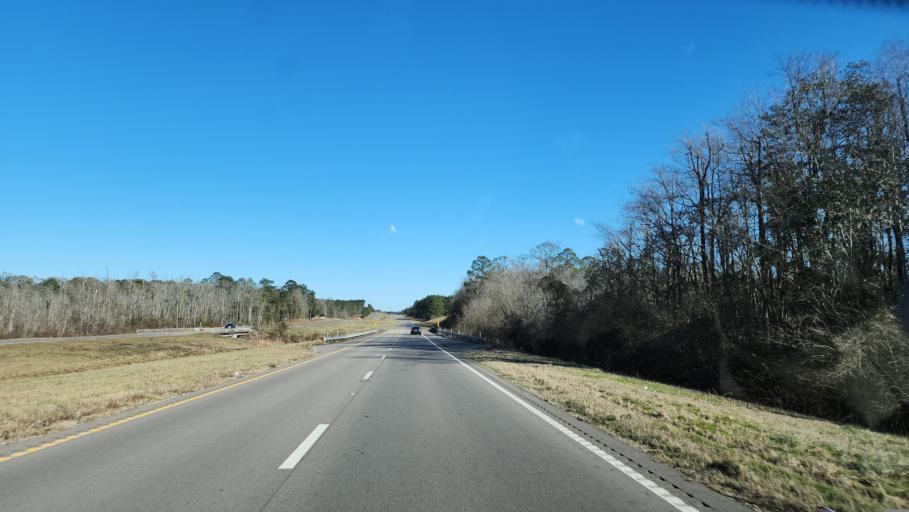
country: US
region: Mississippi
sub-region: Wayne County
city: Waynesboro
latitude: 31.6964
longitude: -88.8508
